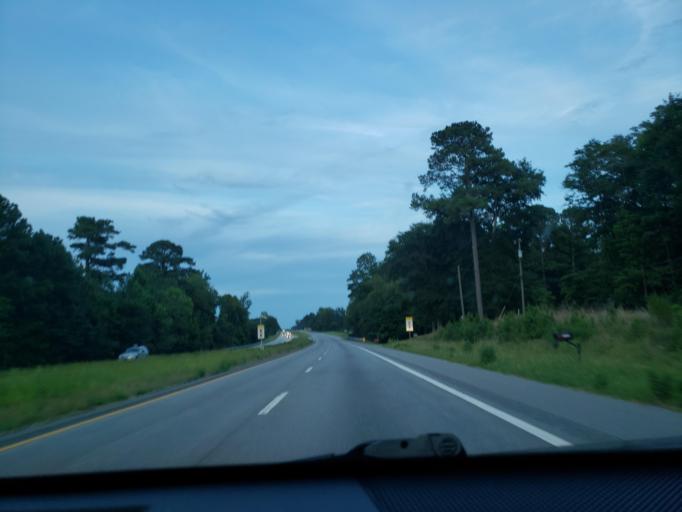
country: US
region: Virginia
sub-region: Southampton County
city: Courtland
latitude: 36.7053
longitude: -77.1939
